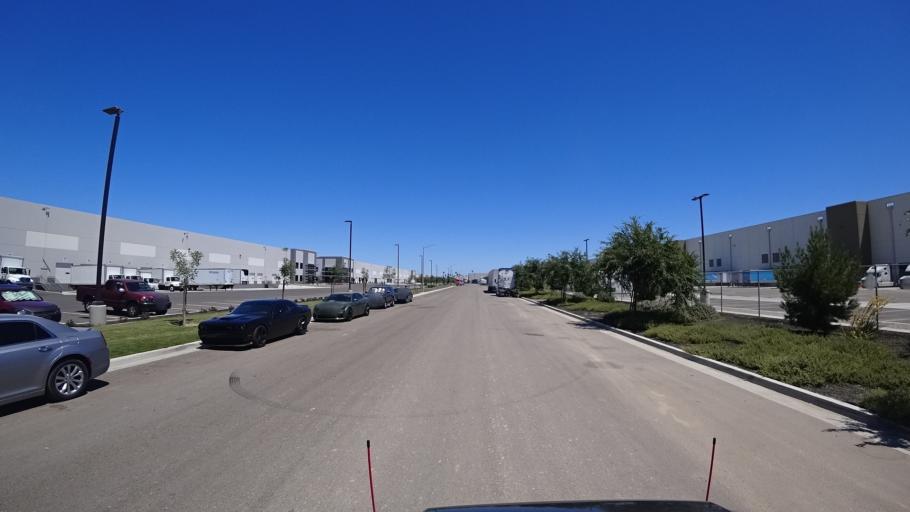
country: US
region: California
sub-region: Fresno County
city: Easton
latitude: 36.6833
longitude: -119.7676
